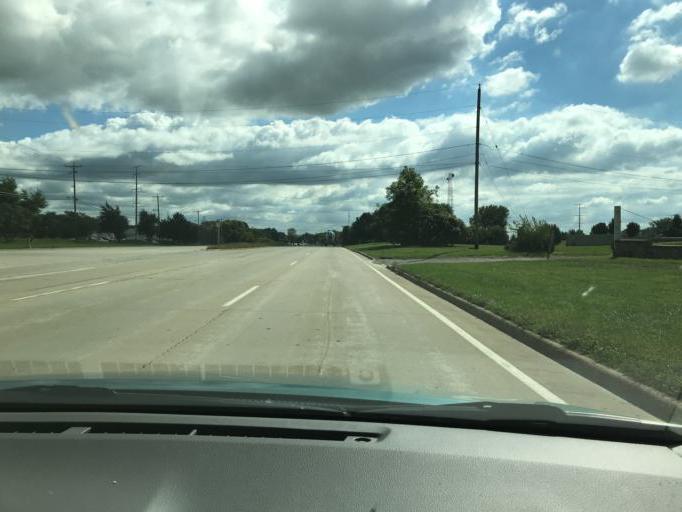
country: US
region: Wisconsin
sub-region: Kenosha County
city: Pleasant Prairie
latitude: 42.5605
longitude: -87.8895
